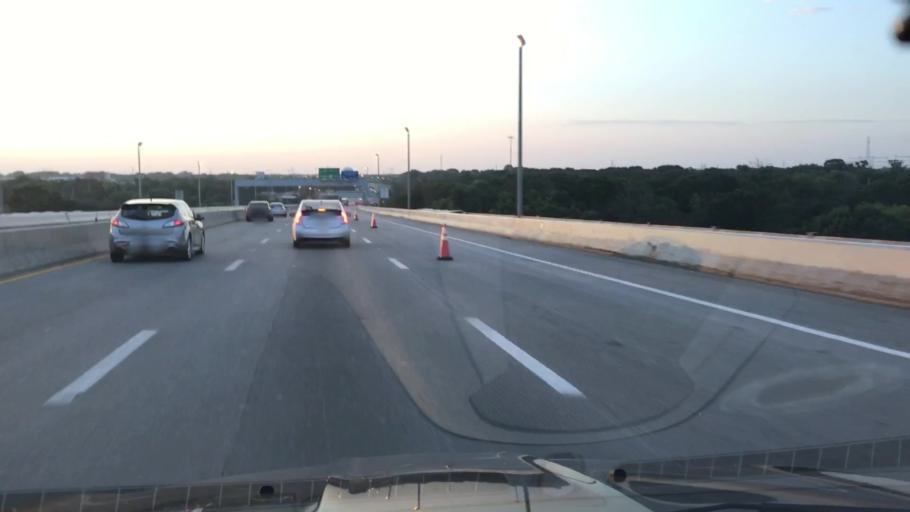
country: US
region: New Jersey
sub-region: Camden County
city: Pennsauken
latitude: 39.9823
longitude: -75.0601
